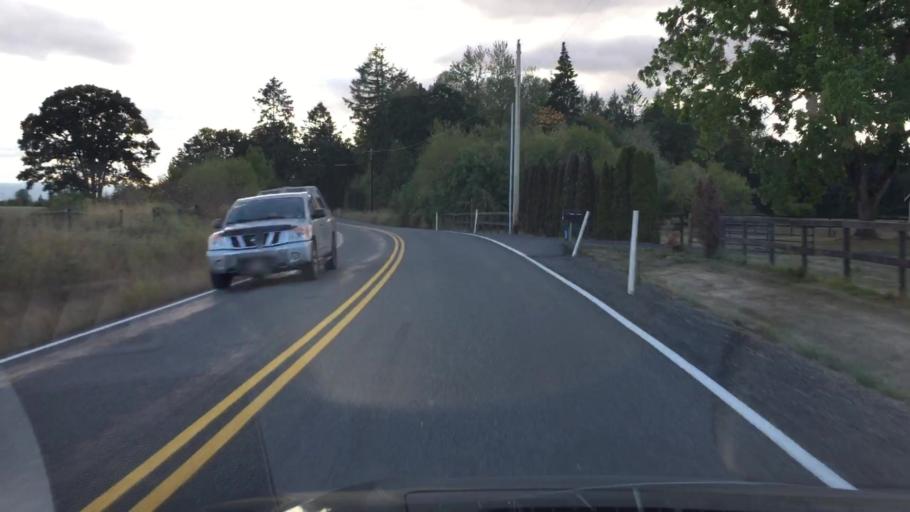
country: US
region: Washington
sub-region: Lewis County
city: Napavine
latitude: 46.4930
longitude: -122.7760
